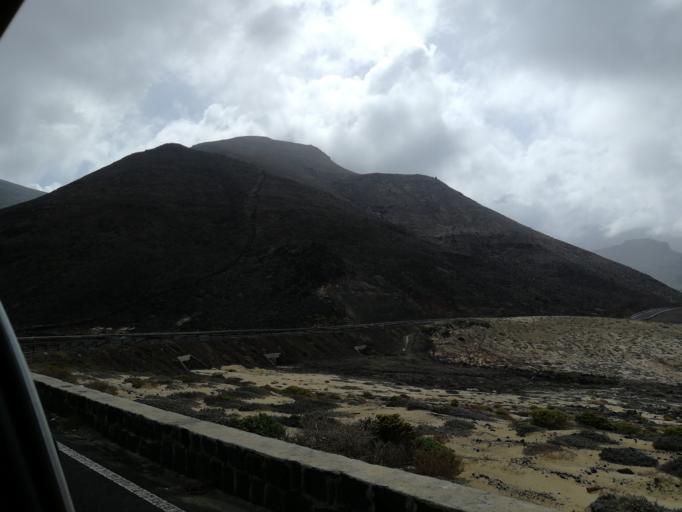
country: CV
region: Sao Vicente
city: Mindelo
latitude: 16.8604
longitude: -24.8887
